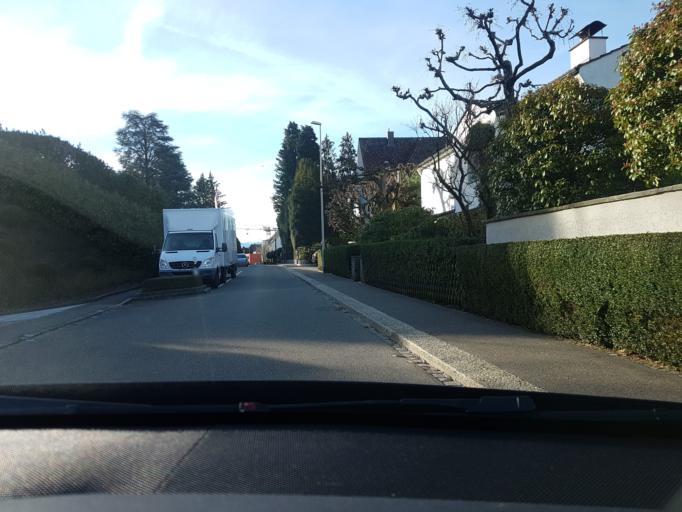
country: CH
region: Zurich
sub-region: Bezirk Meilen
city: Kuesnacht / Goldbach
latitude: 47.3301
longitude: 8.5748
